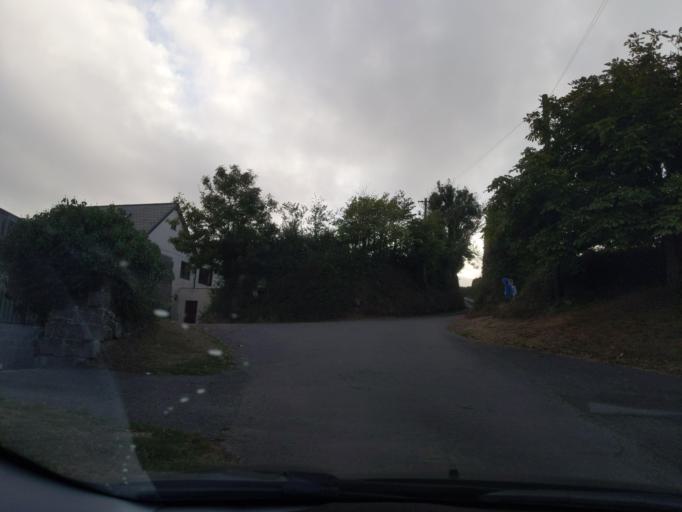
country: GB
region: England
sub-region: Devon
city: Salcombe
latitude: 50.2305
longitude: -3.8049
